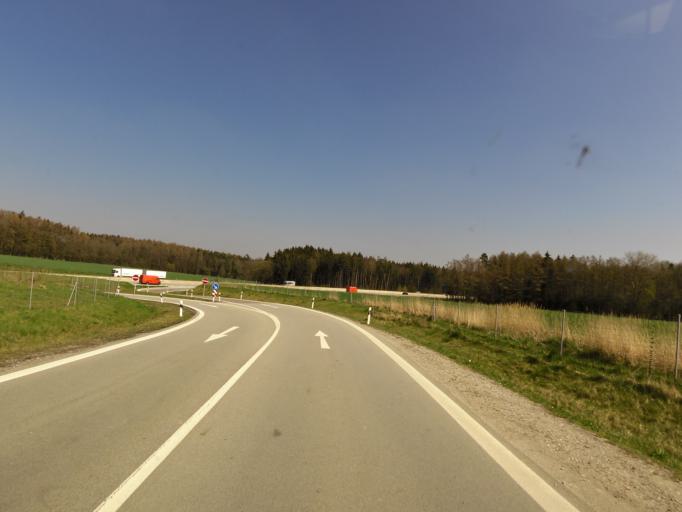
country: DE
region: Bavaria
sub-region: Upper Bavaria
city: Sulzemoos
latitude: 48.2784
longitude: 11.2716
